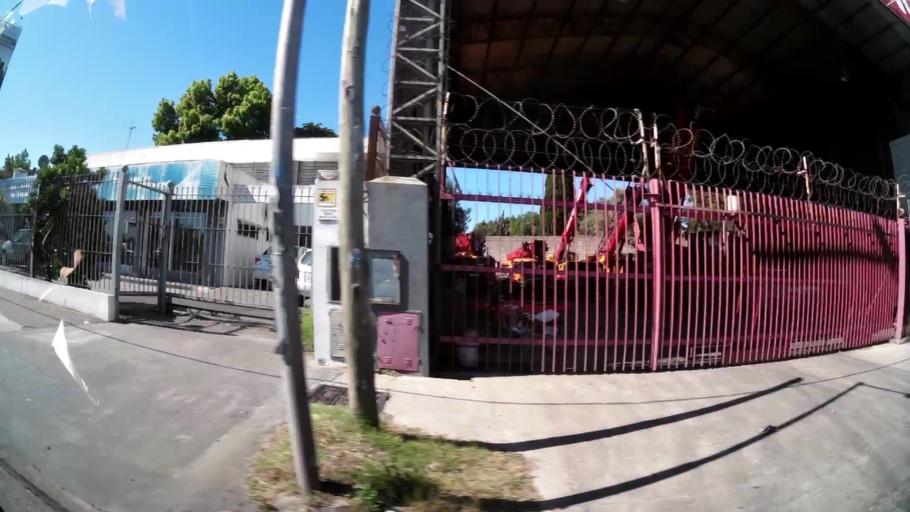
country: AR
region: Buenos Aires
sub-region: Partido de Tigre
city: Tigre
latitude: -34.4844
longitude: -58.6246
